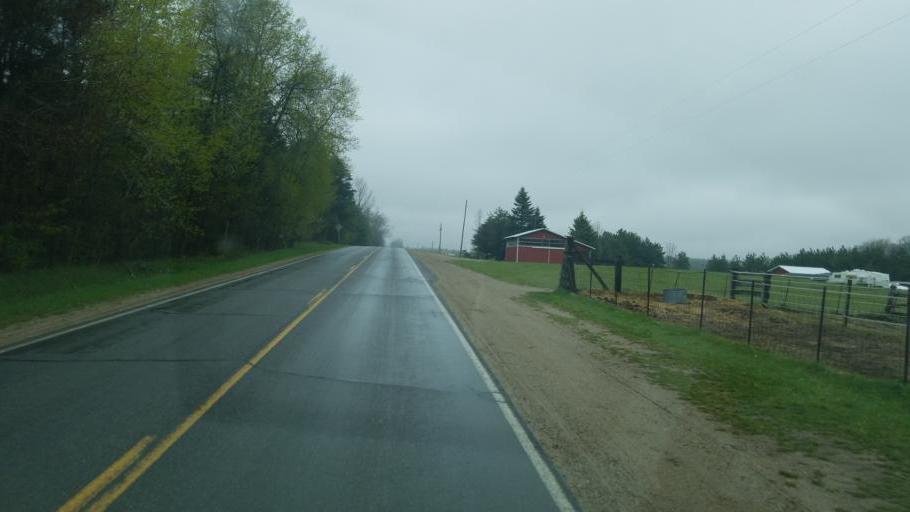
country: US
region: Michigan
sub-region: Mecosta County
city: Canadian Lakes
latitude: 43.5779
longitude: -85.3935
